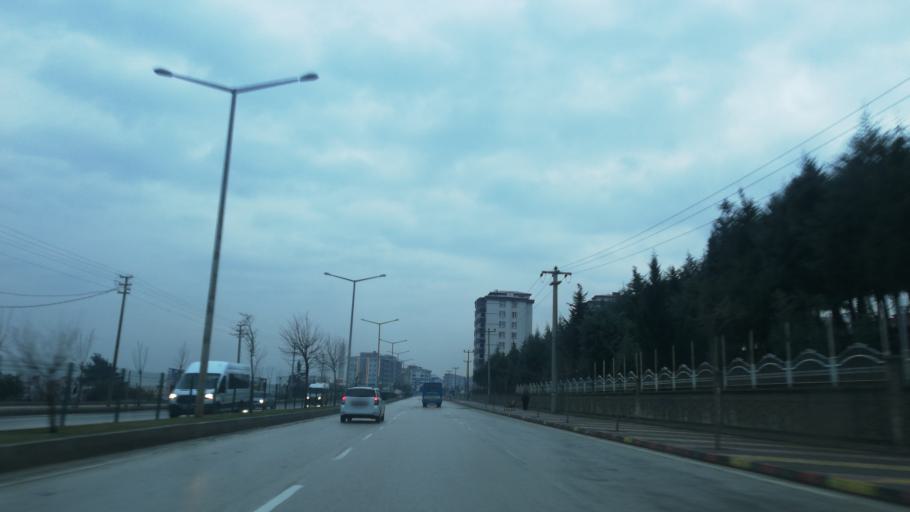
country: TR
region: Kahramanmaras
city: Kahramanmaras
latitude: 37.5832
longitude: 36.9785
